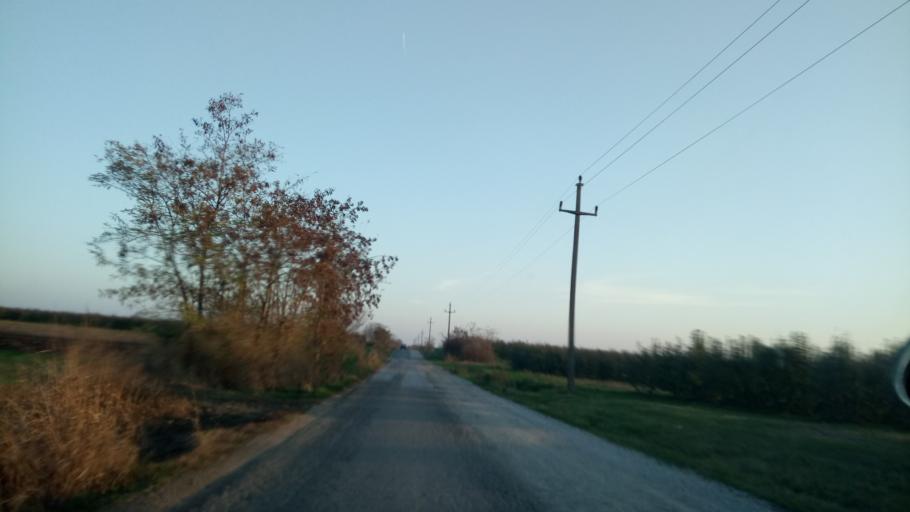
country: RS
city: Novi Slankamen
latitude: 45.1264
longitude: 20.2602
